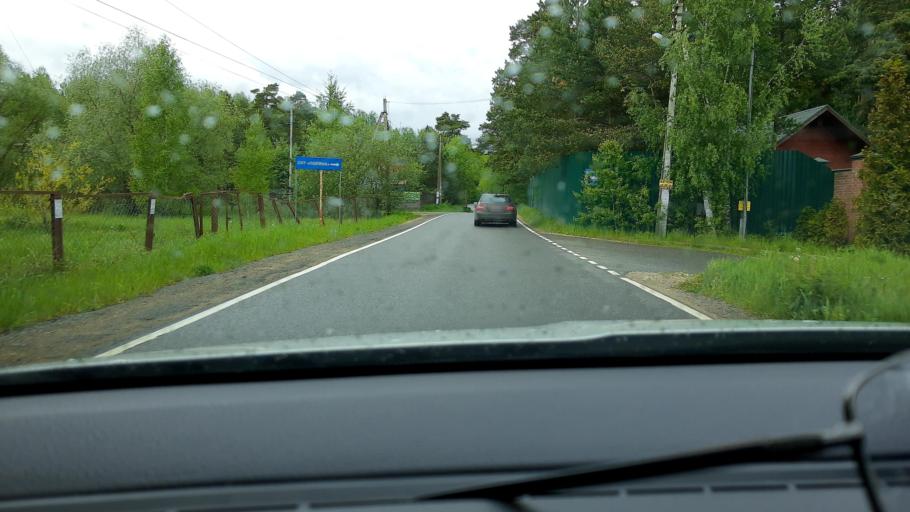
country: RU
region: Moskovskaya
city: Nikolina Gora
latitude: 55.7588
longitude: 36.9815
